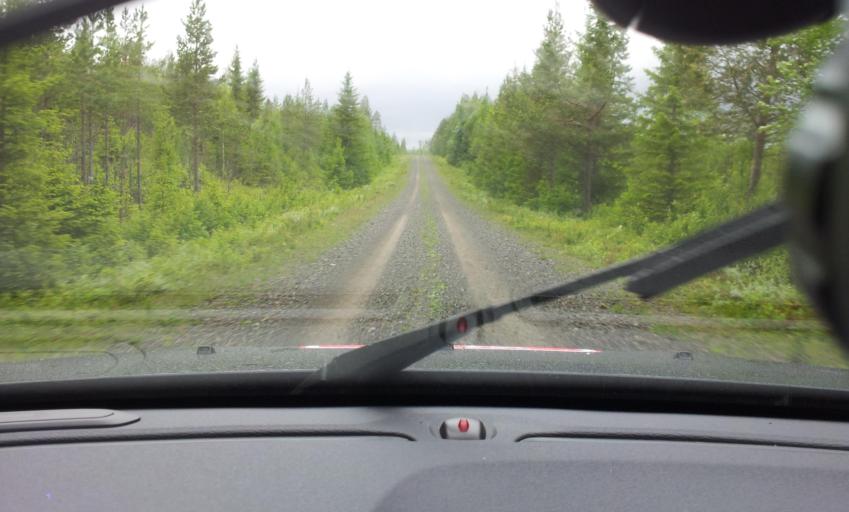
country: SE
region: Jaemtland
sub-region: Are Kommun
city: Jarpen
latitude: 63.2081
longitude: 13.3401
